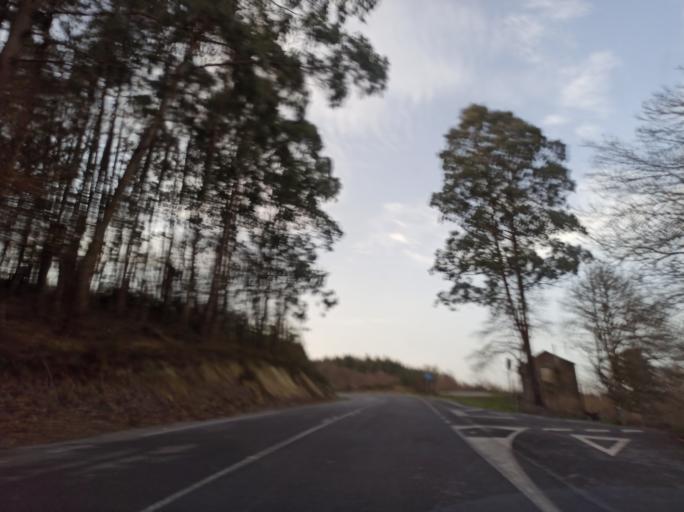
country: ES
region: Galicia
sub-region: Provincia de Lugo
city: Friol
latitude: 43.0267
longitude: -7.8828
